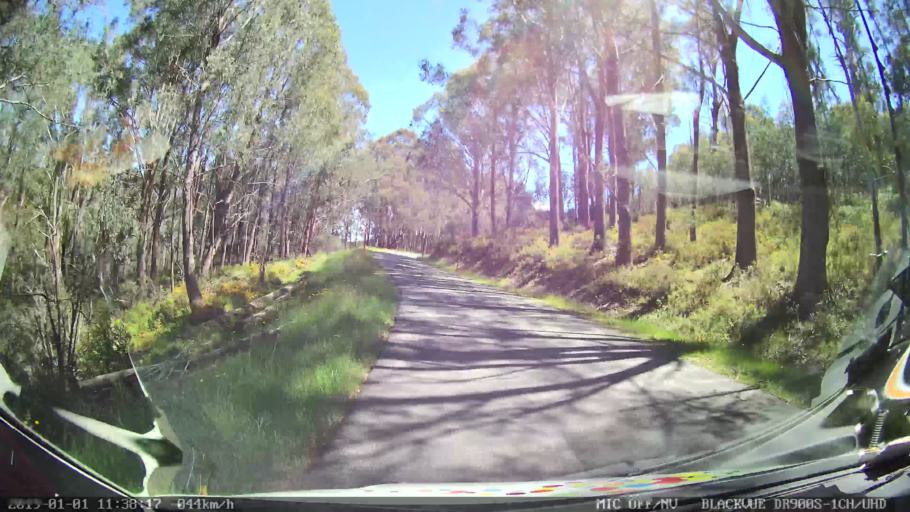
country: AU
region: New South Wales
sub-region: Snowy River
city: Jindabyne
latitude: -35.9352
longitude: 148.3870
